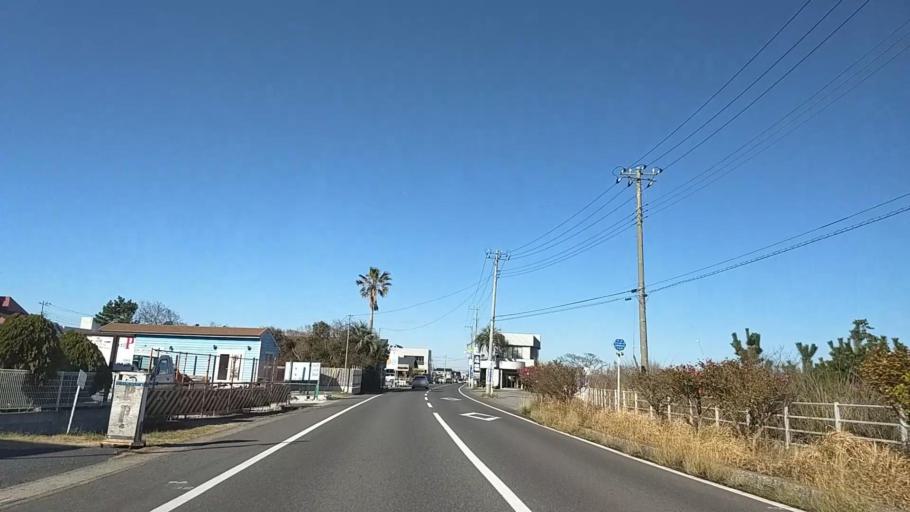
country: JP
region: Chiba
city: Ohara
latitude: 35.3518
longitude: 140.3896
